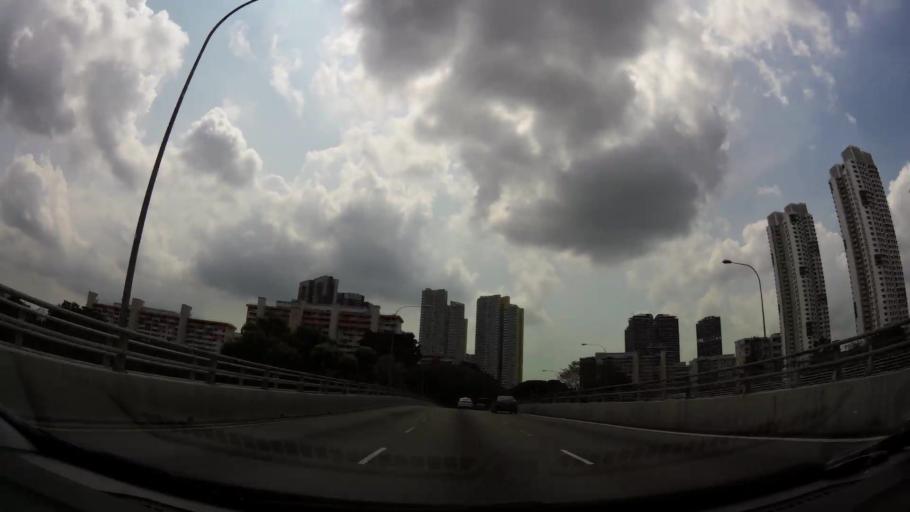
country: SG
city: Singapore
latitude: 1.3238
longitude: 103.7643
